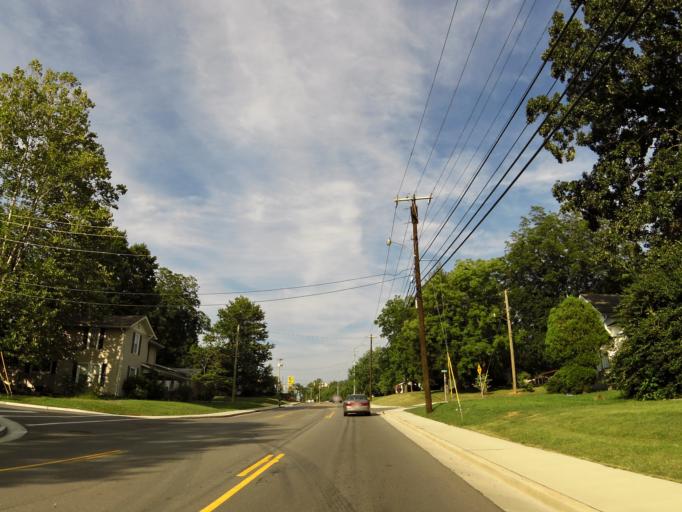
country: US
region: Tennessee
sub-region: Blount County
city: Maryville
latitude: 35.7594
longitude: -83.9521
